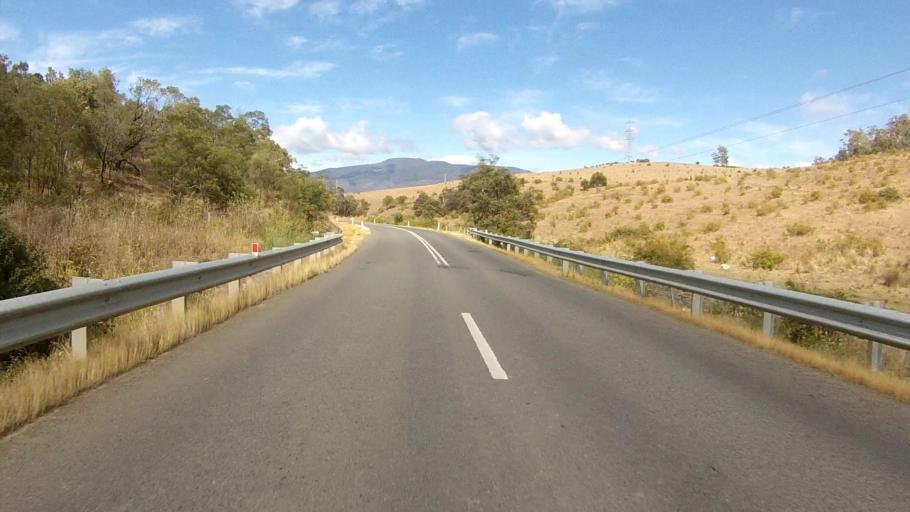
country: AU
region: Tasmania
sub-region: Brighton
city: Old Beach
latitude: -42.7424
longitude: 147.2853
